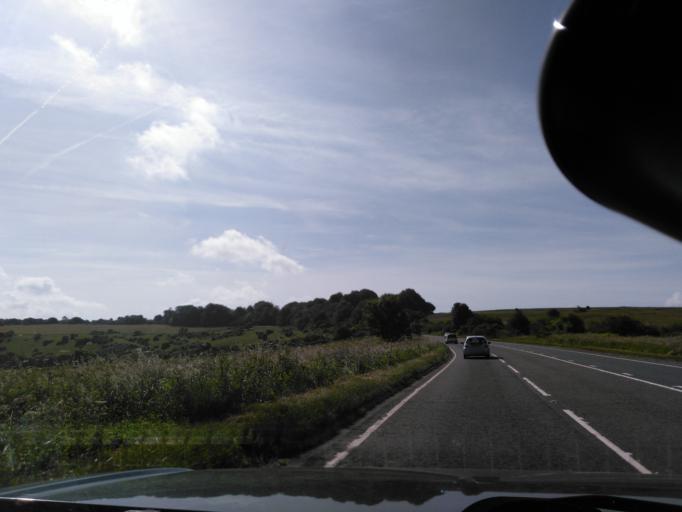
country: GB
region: England
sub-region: Wiltshire
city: Alderbury
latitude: 51.0250
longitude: -1.7091
